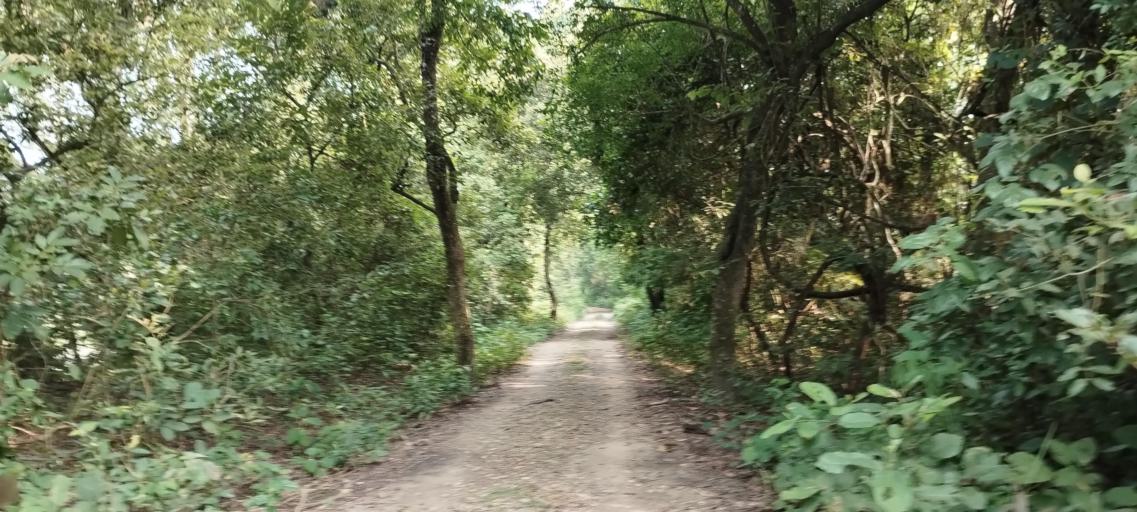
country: NP
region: Far Western
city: Tikapur
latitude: 28.4589
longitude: 81.2420
